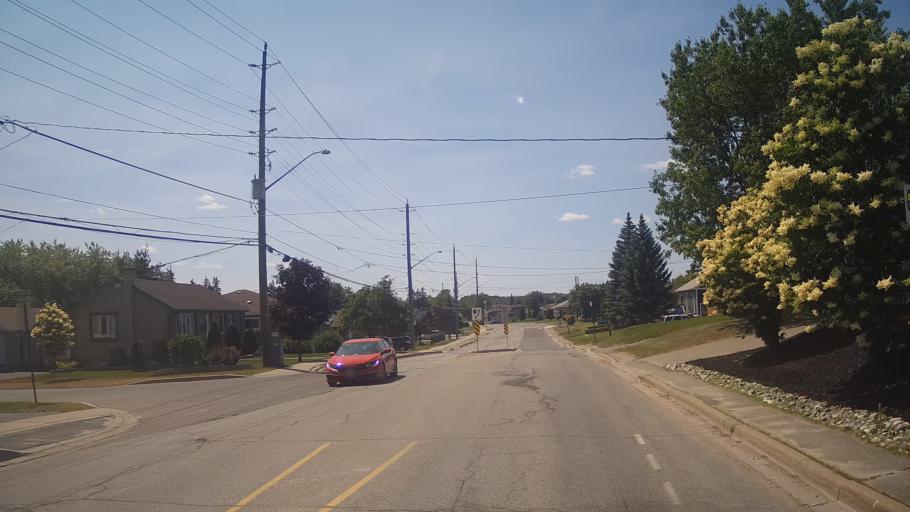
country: CA
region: Ontario
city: Greater Sudbury
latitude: 46.4598
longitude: -81.0238
